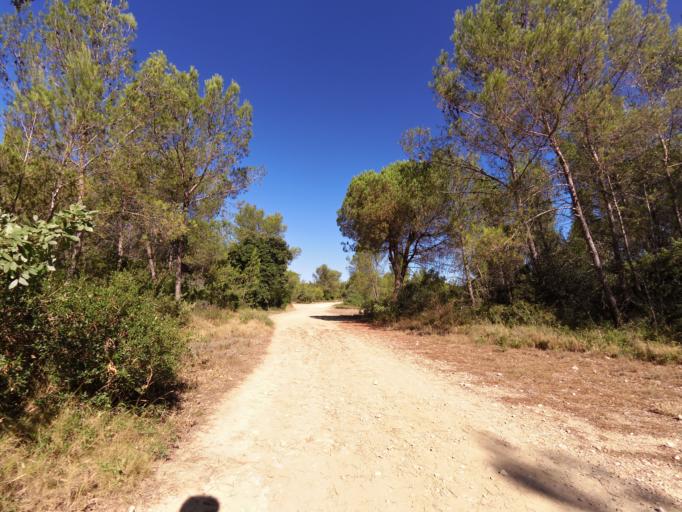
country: FR
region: Languedoc-Roussillon
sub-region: Departement du Gard
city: Congenies
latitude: 43.7603
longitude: 4.1889
